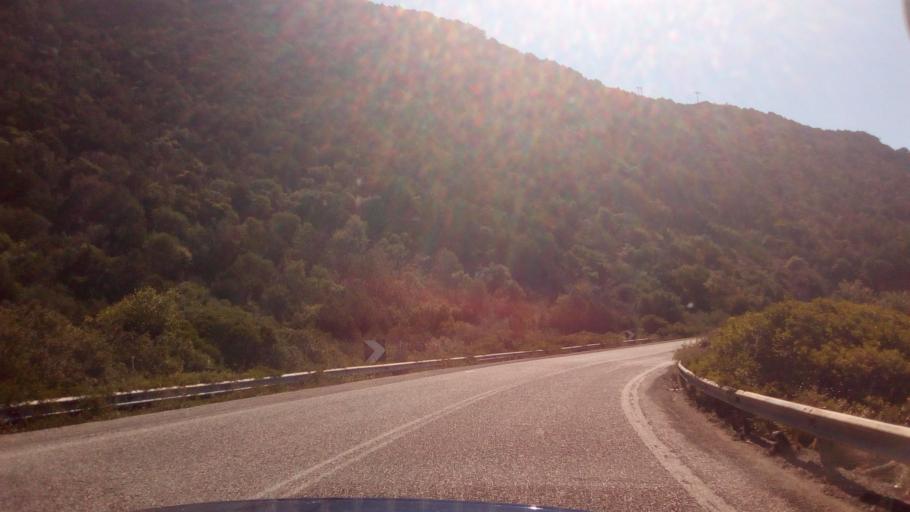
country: GR
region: West Greece
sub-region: Nomos Achaias
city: Selianitika
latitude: 38.3755
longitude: 22.0977
